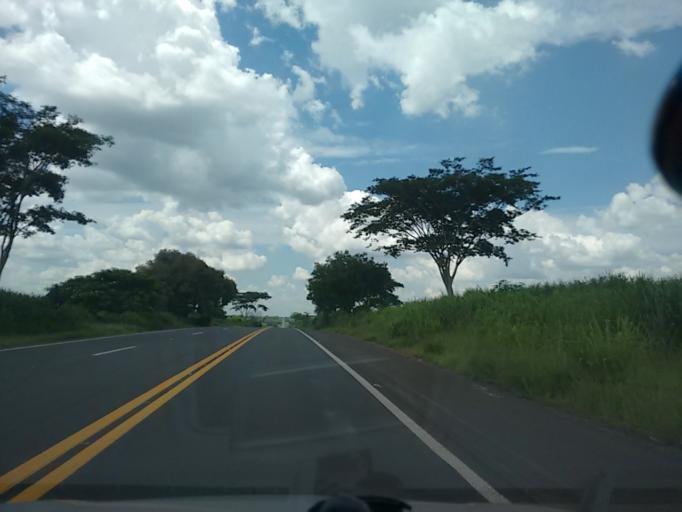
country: BR
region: Sao Paulo
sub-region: Osvaldo Cruz
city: Osvaldo Cruz
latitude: -21.8958
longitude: -50.8778
